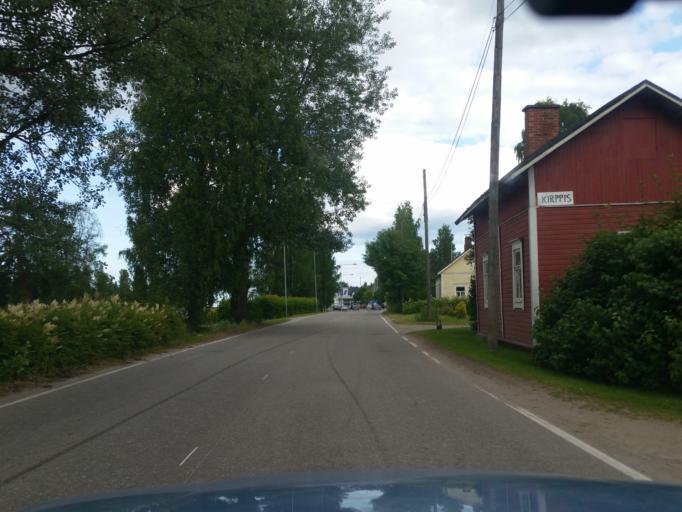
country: FI
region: Southern Savonia
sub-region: Savonlinna
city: Sulkava
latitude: 61.7889
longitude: 28.3672
